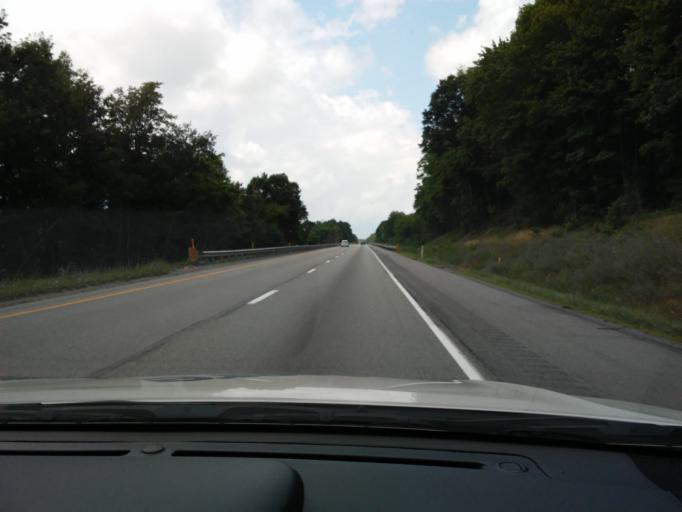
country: US
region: Pennsylvania
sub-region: Clearfield County
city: Troy
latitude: 40.9676
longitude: -78.1141
